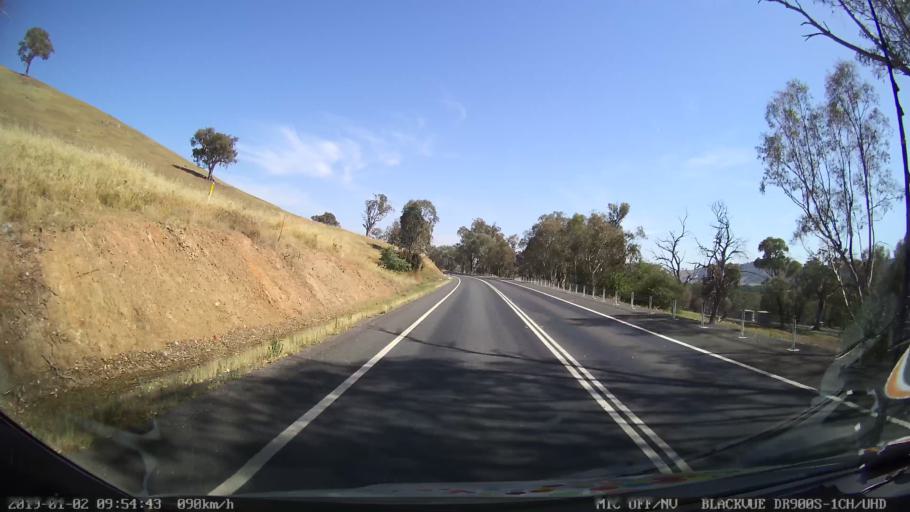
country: AU
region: New South Wales
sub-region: Tumut Shire
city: Tumut
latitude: -35.2316
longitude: 148.1952
